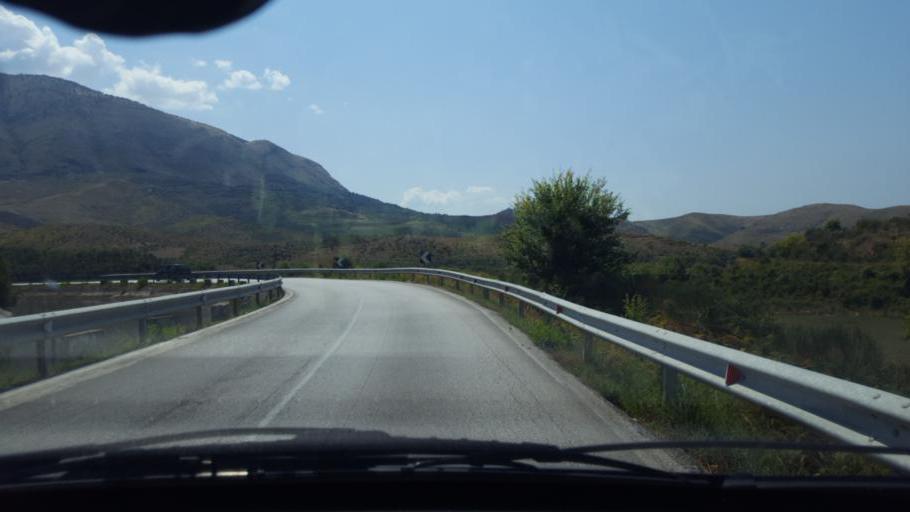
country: AL
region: Vlore
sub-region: Rrethi i Delvines
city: Mesopotam
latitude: 39.9091
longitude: 20.1232
